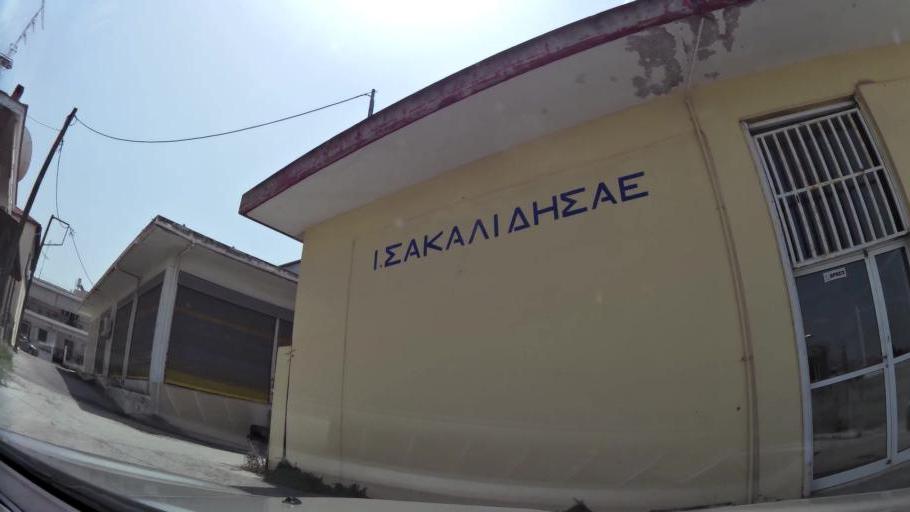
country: GR
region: Central Macedonia
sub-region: Nomos Thessalonikis
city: Evosmos
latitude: 40.6752
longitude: 22.8921
